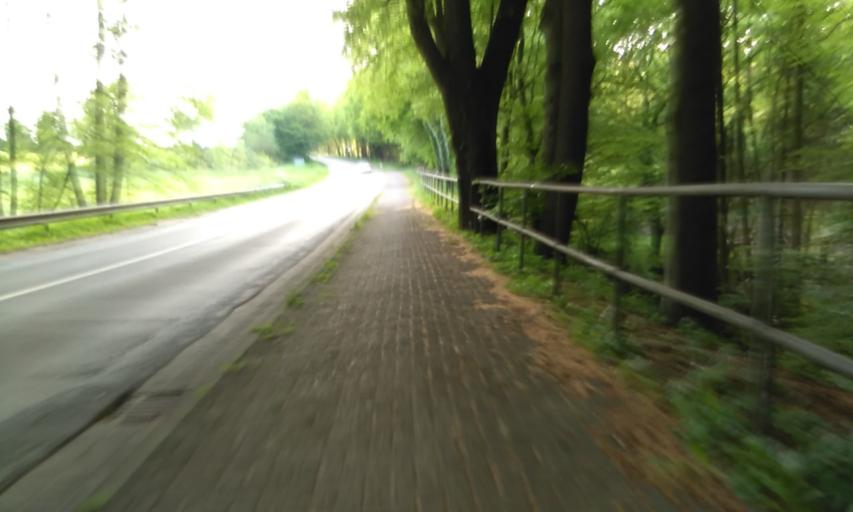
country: DE
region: Lower Saxony
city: Bliedersdorf
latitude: 53.4640
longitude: 9.5502
